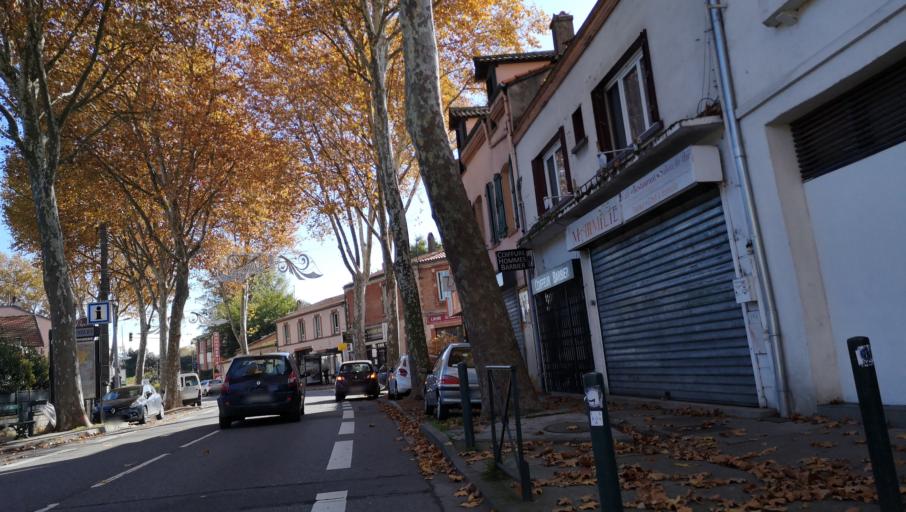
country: FR
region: Midi-Pyrenees
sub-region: Departement de la Haute-Garonne
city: Blagnac
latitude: 43.6121
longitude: 1.4135
